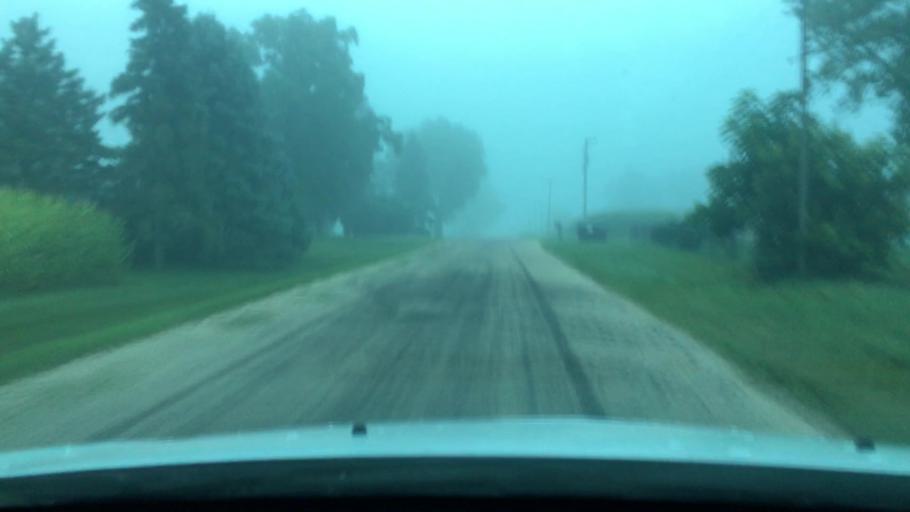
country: US
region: Illinois
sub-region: Ogle County
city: Rochelle
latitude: 41.8698
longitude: -88.9813
